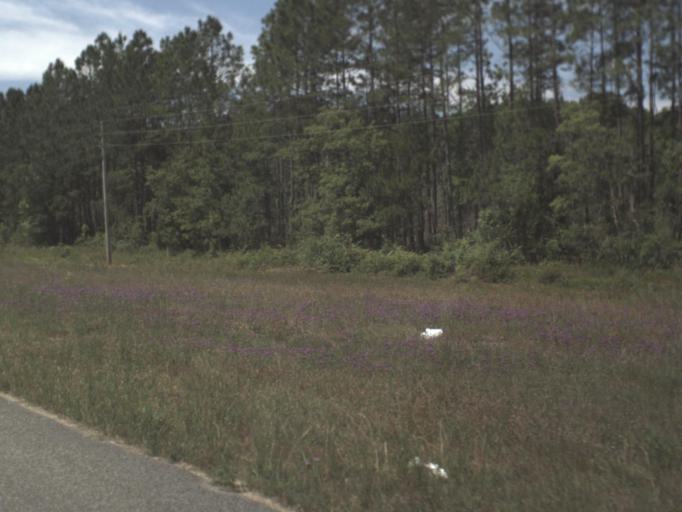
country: US
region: Florida
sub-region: Jackson County
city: Marianna
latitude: 30.6924
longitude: -85.2347
